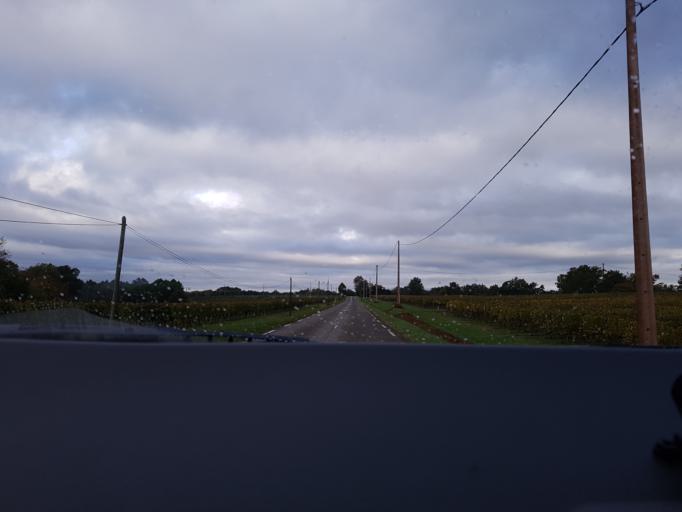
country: FR
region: Midi-Pyrenees
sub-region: Departement du Gers
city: Cazaubon
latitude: 43.9364
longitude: -0.1239
